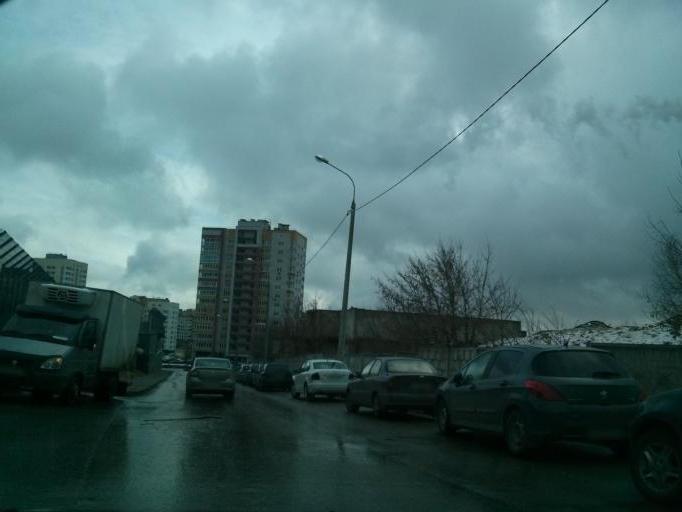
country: RU
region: Nizjnij Novgorod
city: Afonino
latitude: 56.3069
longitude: 44.0725
